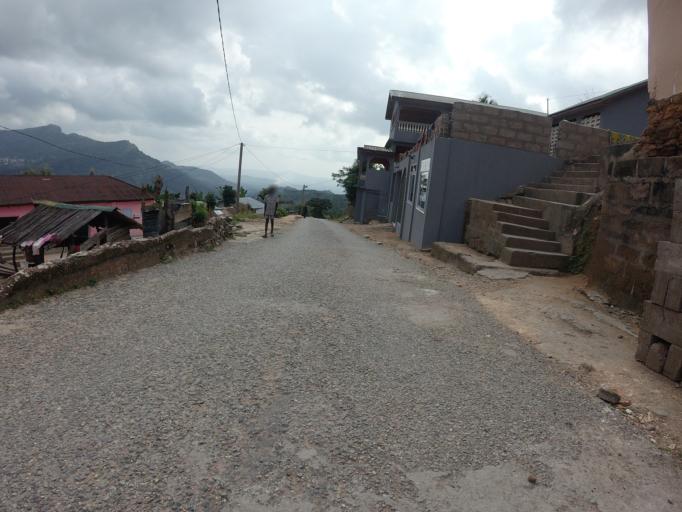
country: TG
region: Plateaux
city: Kpalime
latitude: 6.8890
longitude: 0.4567
